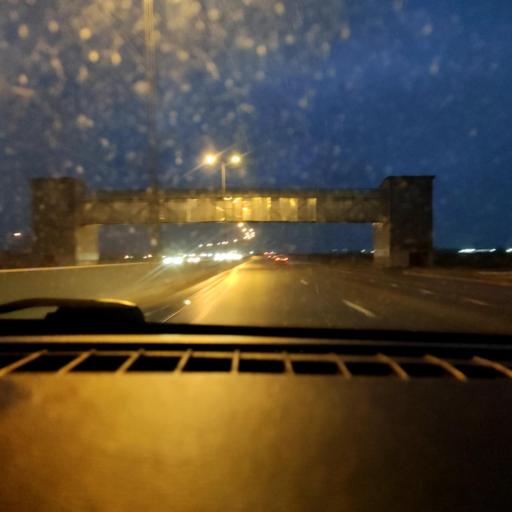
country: RU
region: Perm
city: Kondratovo
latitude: 57.9338
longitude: 56.1623
